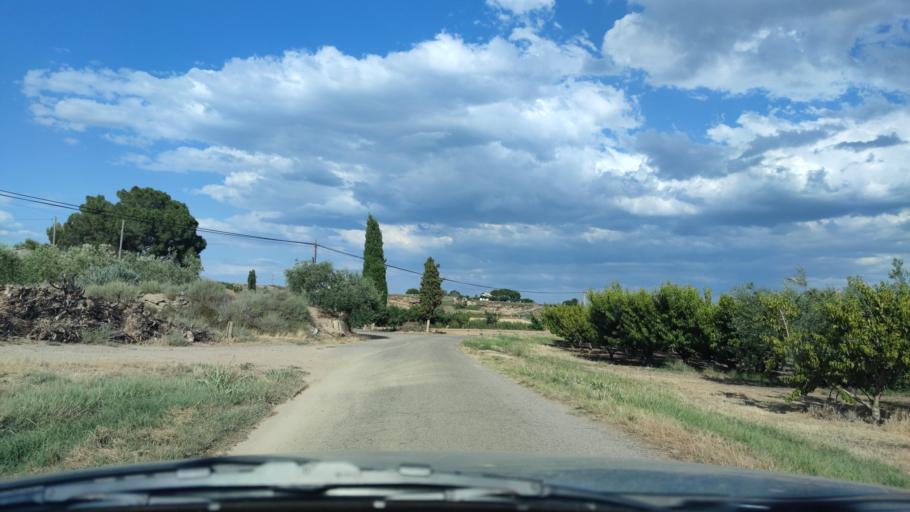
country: ES
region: Catalonia
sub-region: Provincia de Lleida
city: Alpicat
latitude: 41.6322
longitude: 0.5551
